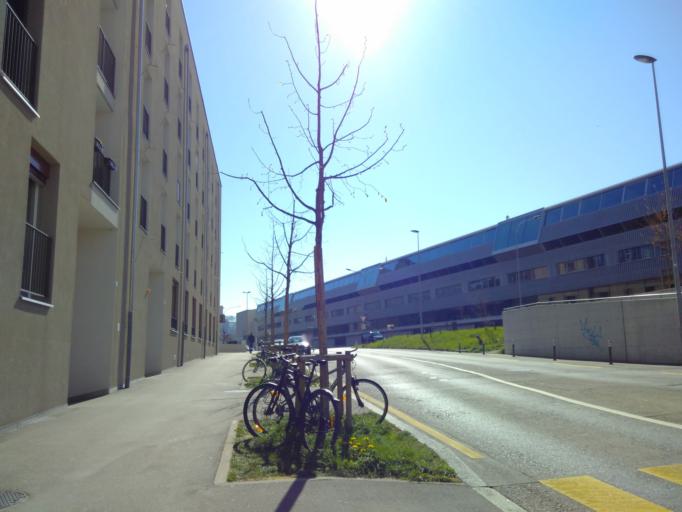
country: CH
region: Fribourg
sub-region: Sarine District
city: Fribourg
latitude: 46.7948
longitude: 7.1549
